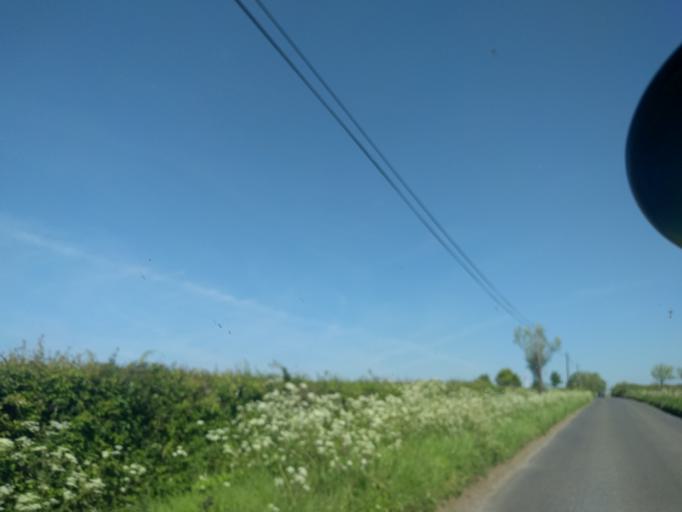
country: GB
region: England
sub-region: Somerset
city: Langport
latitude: 51.0607
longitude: -2.8222
